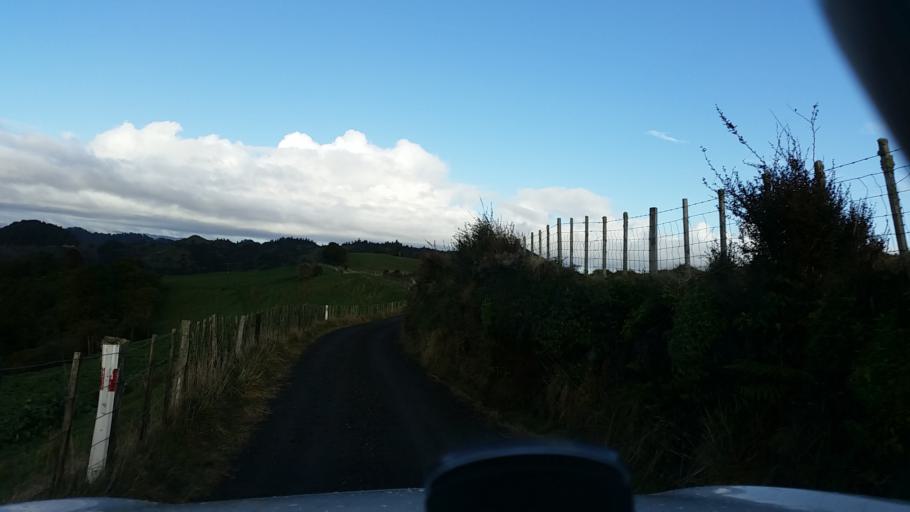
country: NZ
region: Taranaki
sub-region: South Taranaki District
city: Eltham
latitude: -39.4105
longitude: 174.5687
